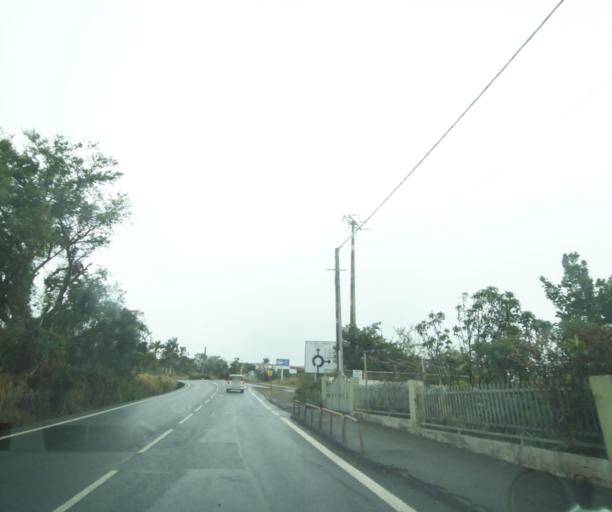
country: RE
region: Reunion
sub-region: Reunion
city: Saint-Paul
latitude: -21.0427
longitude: 55.2676
